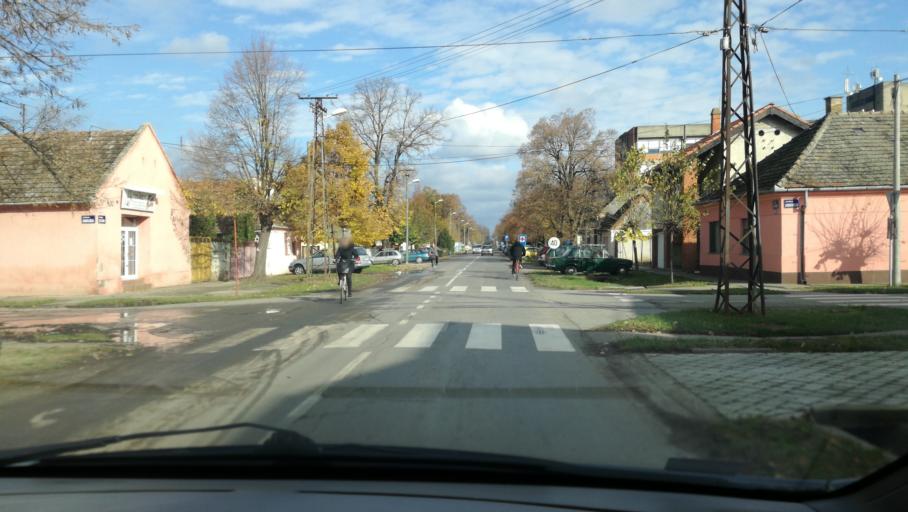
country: RS
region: Autonomna Pokrajina Vojvodina
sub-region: Severnobanatski Okrug
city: Kikinda
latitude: 45.8326
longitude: 20.4764
